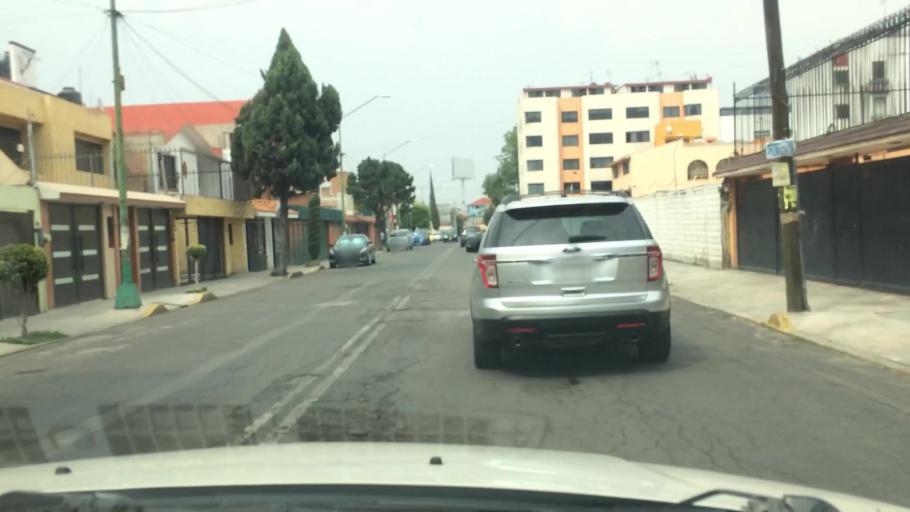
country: MX
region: Mexico City
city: Xochimilco
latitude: 19.2737
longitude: -99.1224
